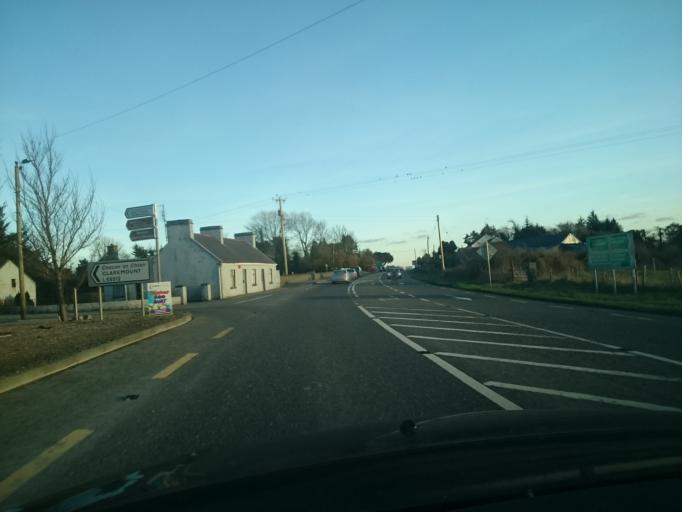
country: IE
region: Connaught
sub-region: Maigh Eo
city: Claremorris
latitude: 53.7371
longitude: -9.0078
